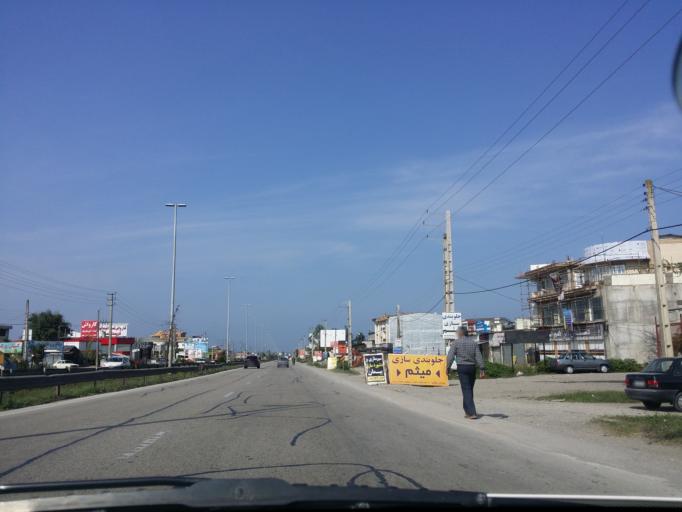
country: IR
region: Mazandaran
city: Chalus
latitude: 36.6625
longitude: 51.3989
